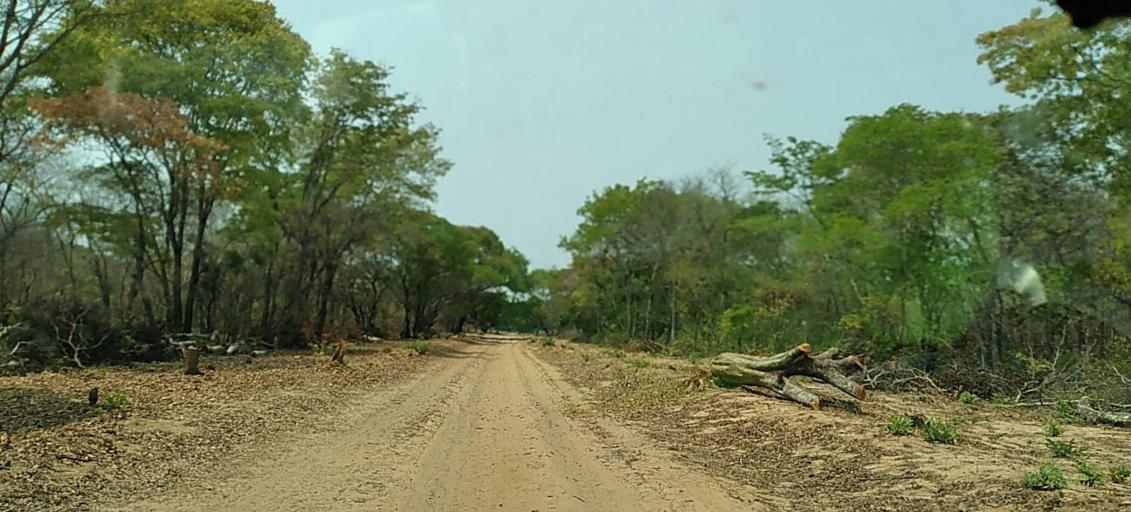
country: ZM
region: Western
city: Lukulu
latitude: -13.9938
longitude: 23.2327
